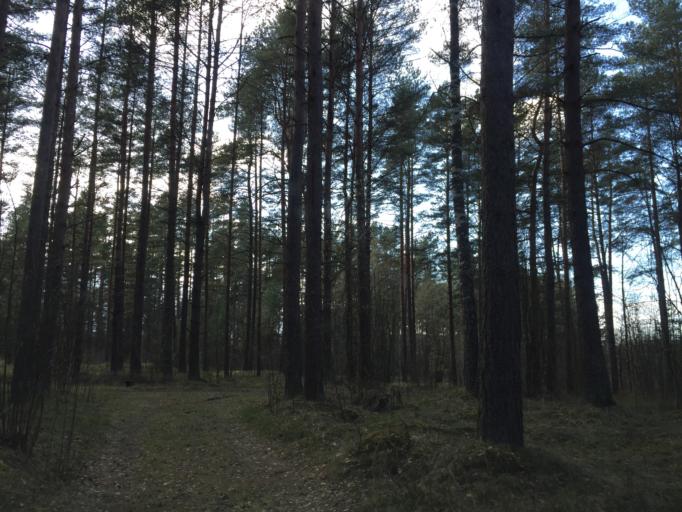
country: LV
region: Riga
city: Bergi
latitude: 57.0024
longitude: 24.2923
